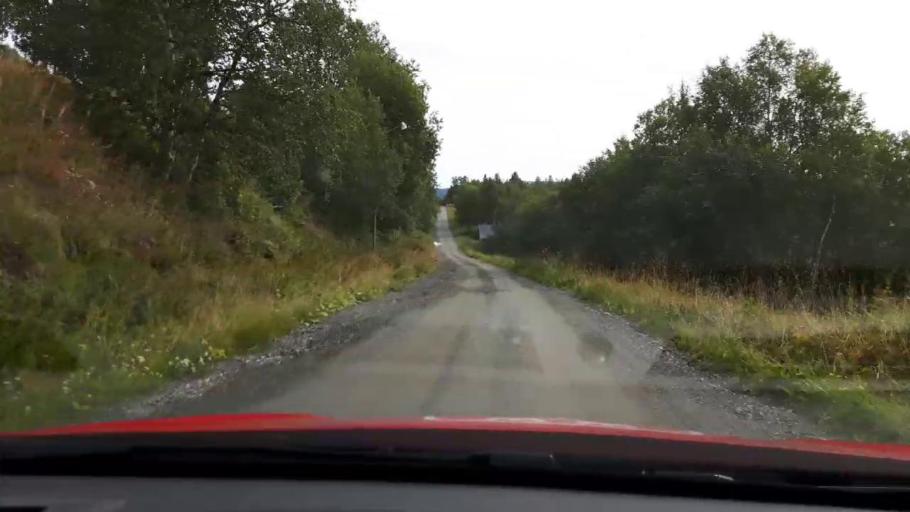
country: SE
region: Jaemtland
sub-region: Are Kommun
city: Are
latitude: 63.7503
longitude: 12.9595
